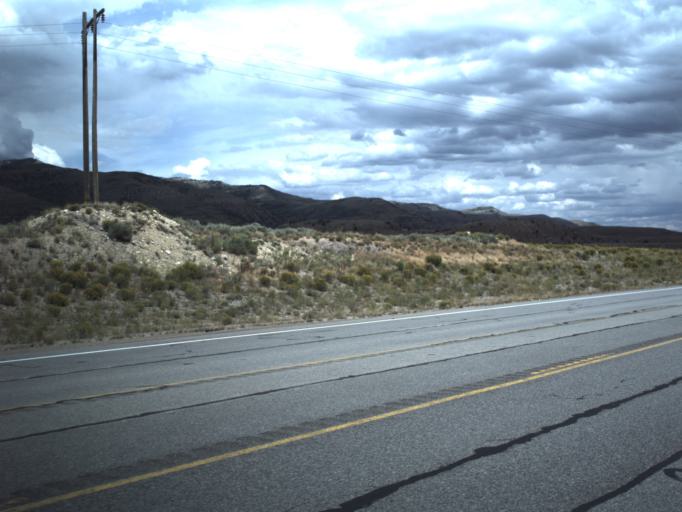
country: US
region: Utah
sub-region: Carbon County
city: Helper
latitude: 39.8306
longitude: -110.9633
